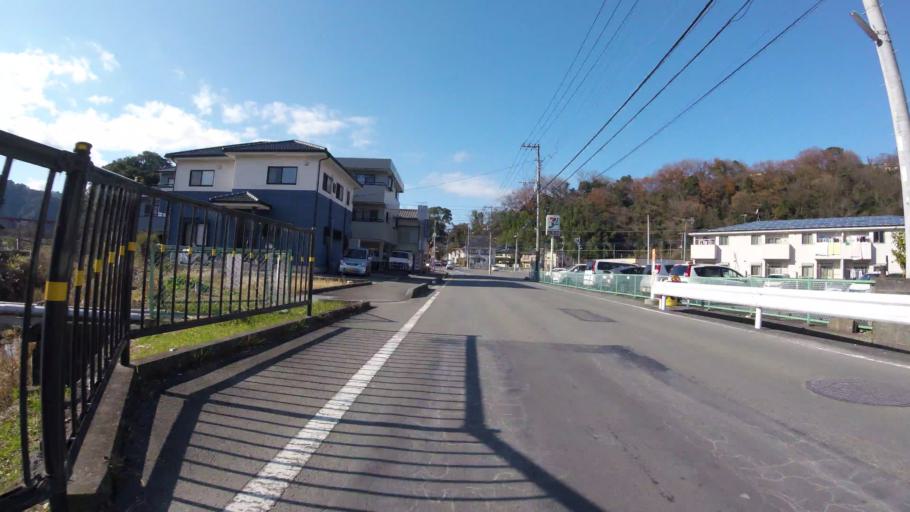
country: JP
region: Shizuoka
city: Mishima
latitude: 34.9928
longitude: 138.9436
